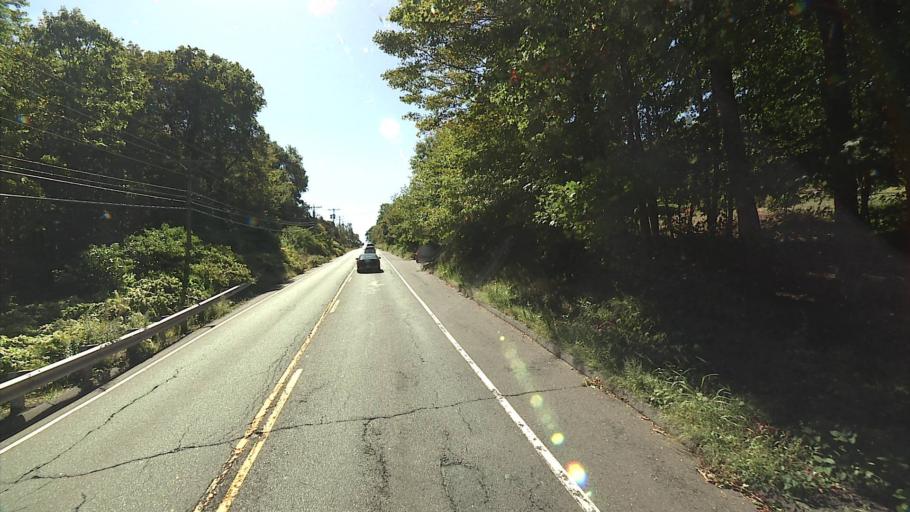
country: US
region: Connecticut
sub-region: New Haven County
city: Prospect
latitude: 41.4769
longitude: -72.9693
